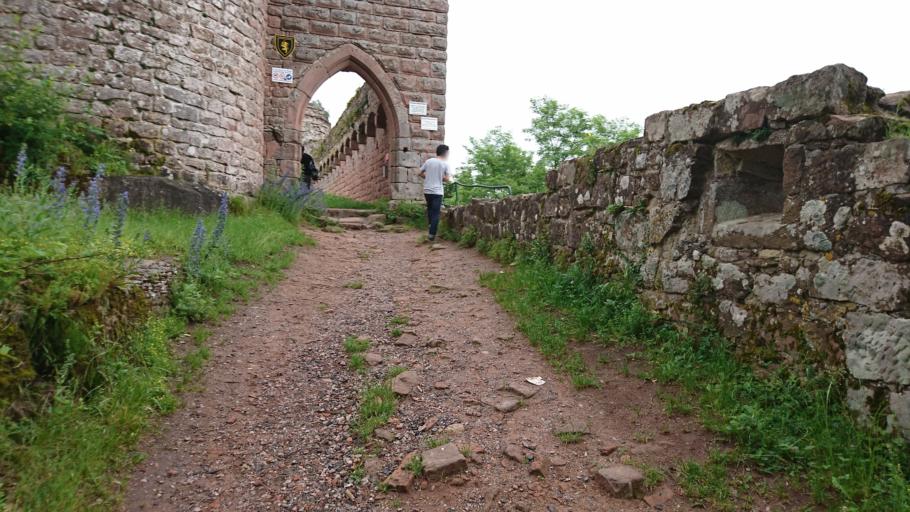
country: DE
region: Rheinland-Pfalz
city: Ramberg
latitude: 49.2525
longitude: 8.0208
